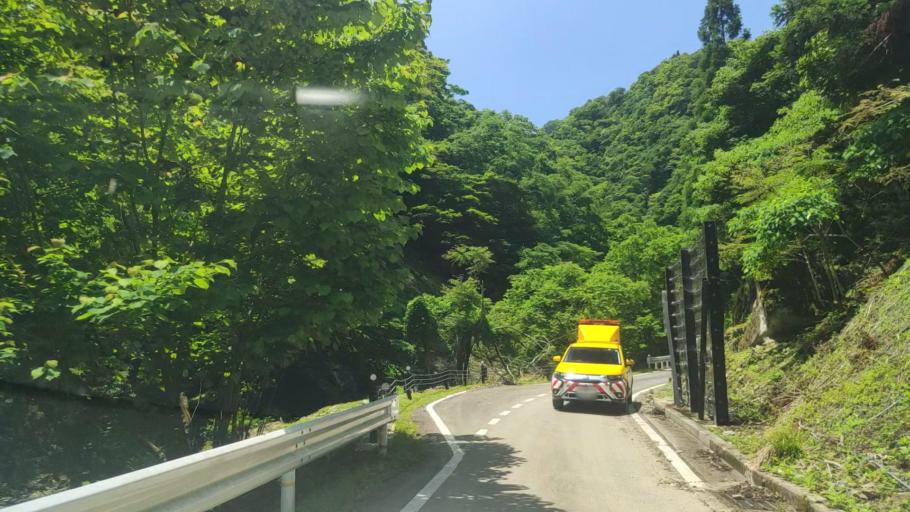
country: JP
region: Tottori
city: Tottori
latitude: 35.4017
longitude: 134.4995
